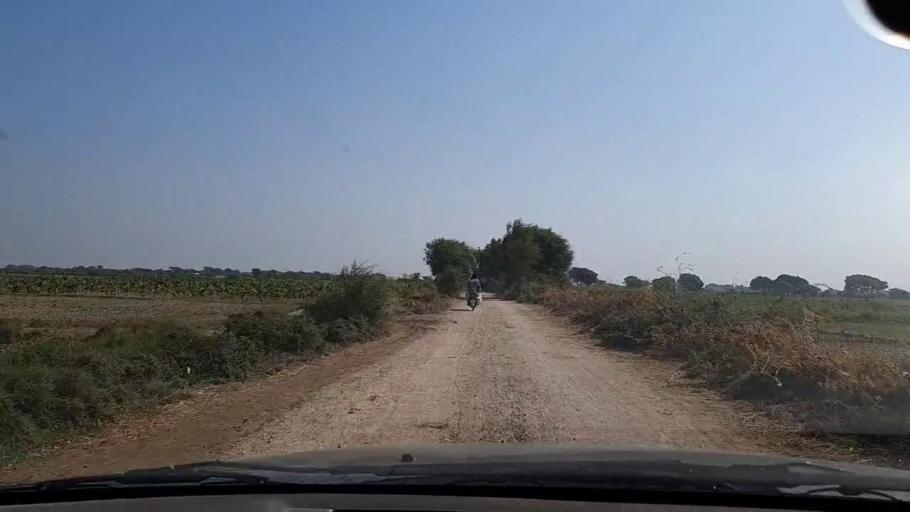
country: PK
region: Sindh
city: Chuhar Jamali
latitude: 24.4185
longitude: 67.8286
